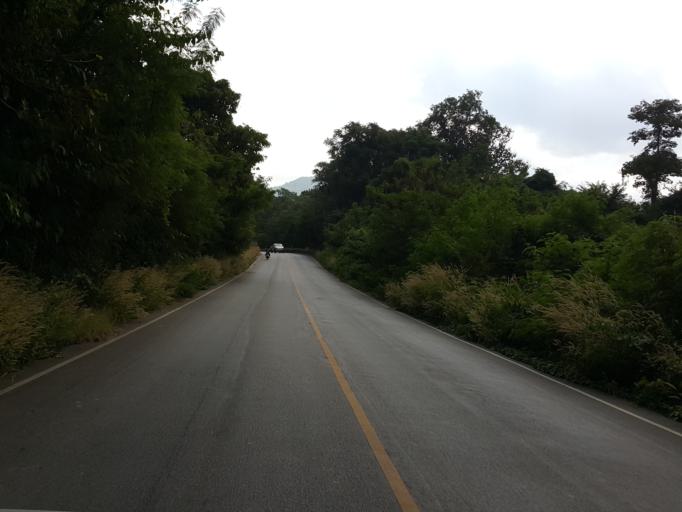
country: TH
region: Sukhothai
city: Thung Saliam
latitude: 17.3372
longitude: 99.4758
